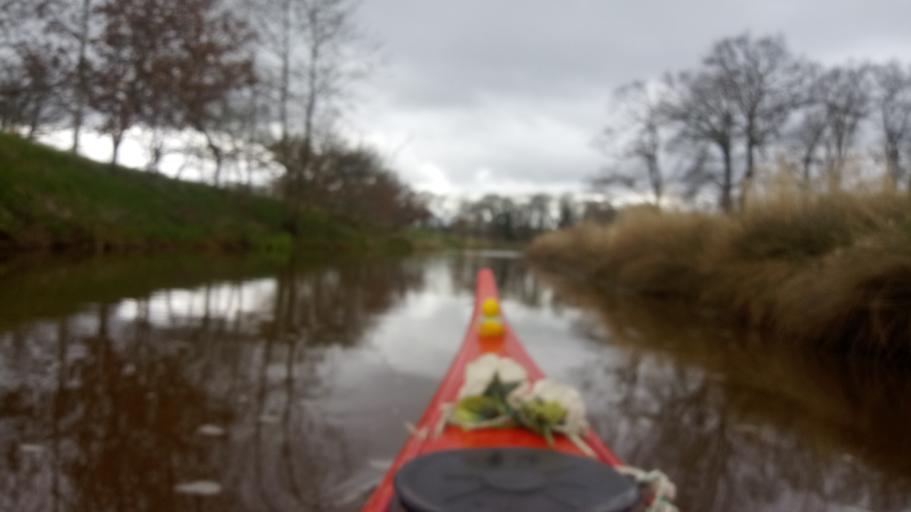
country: NL
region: Groningen
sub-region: Gemeente Vlagtwedde
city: Sellingen
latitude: 52.9288
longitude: 7.1251
